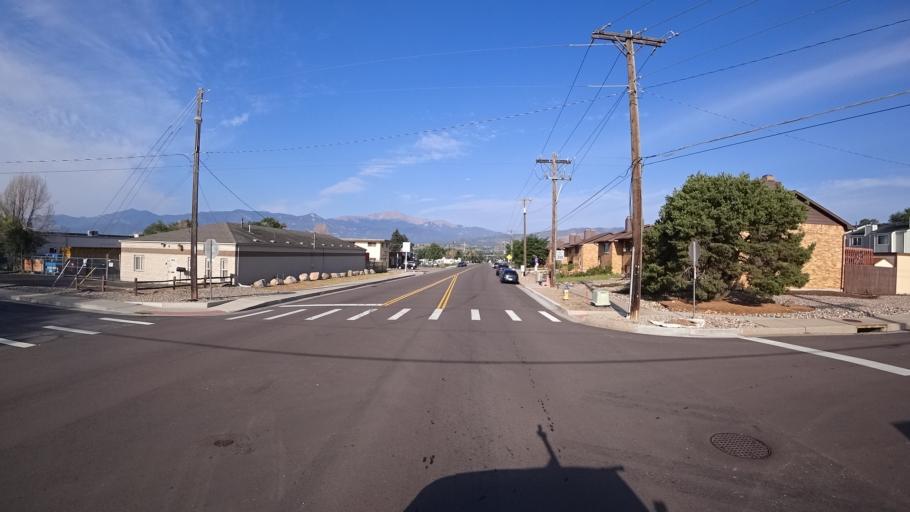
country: US
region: Colorado
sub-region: El Paso County
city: Colorado Springs
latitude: 38.8896
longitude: -104.8126
